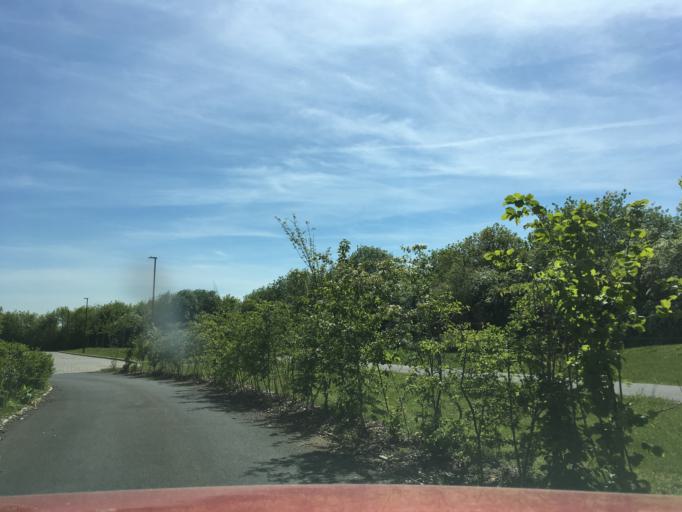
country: GB
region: England
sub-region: Gloucestershire
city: Coates
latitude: 51.6720
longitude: -2.0214
